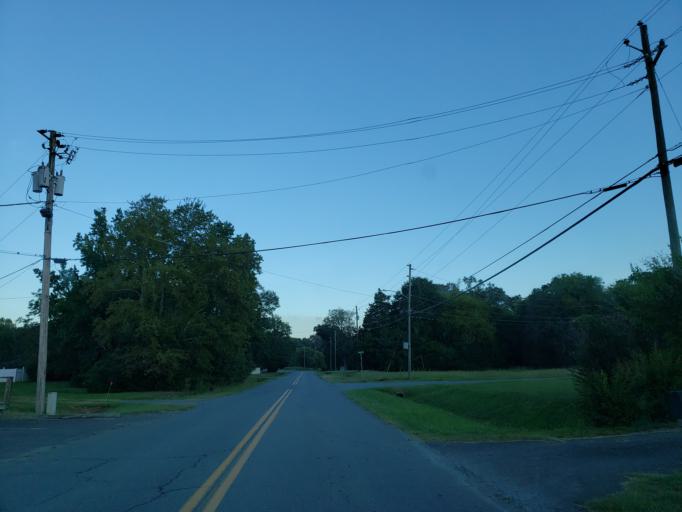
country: US
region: Georgia
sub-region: Floyd County
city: Rome
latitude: 34.2428
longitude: -85.1342
